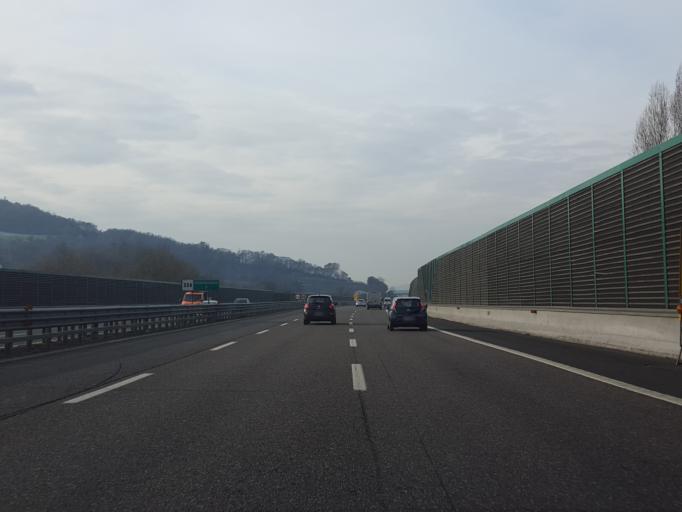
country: IT
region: Veneto
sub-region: Provincia di Vicenza
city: Altavilla Vicentina
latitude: 45.5074
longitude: 11.4712
